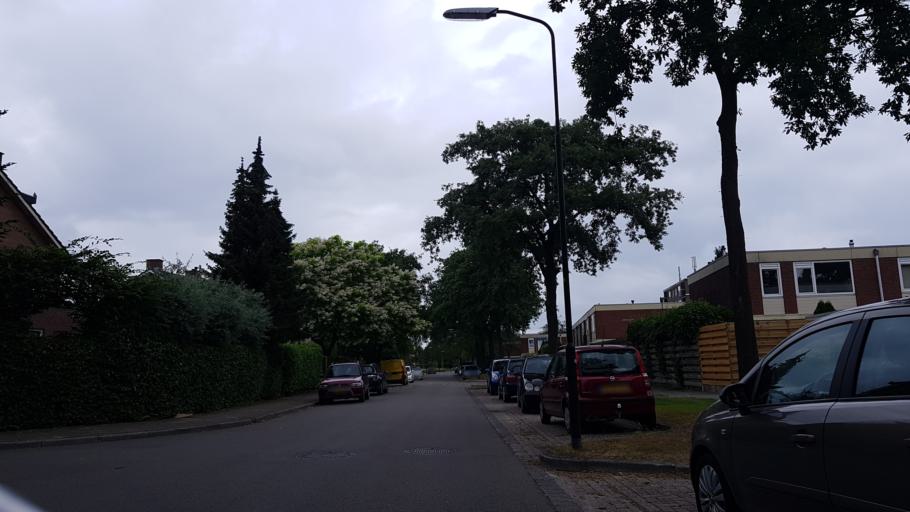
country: NL
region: Gelderland
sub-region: Gemeente Apeldoorn
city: Apeldoorn
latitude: 52.1887
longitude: 5.9756
